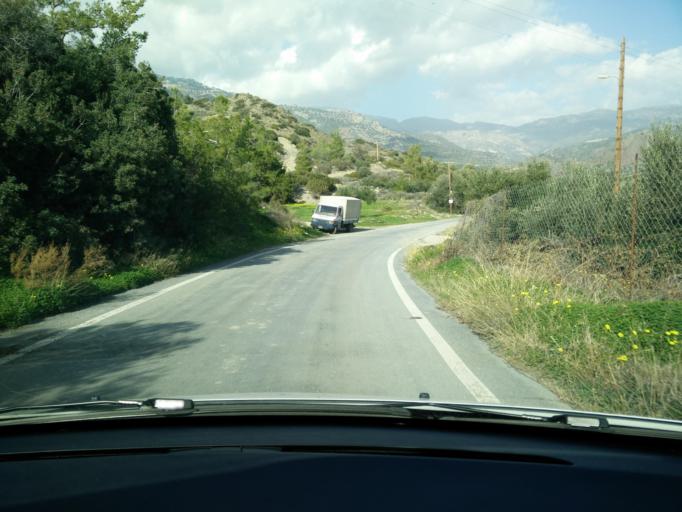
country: GR
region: Crete
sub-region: Nomos Lasithiou
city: Gra Liyia
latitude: 35.0183
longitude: 25.5839
